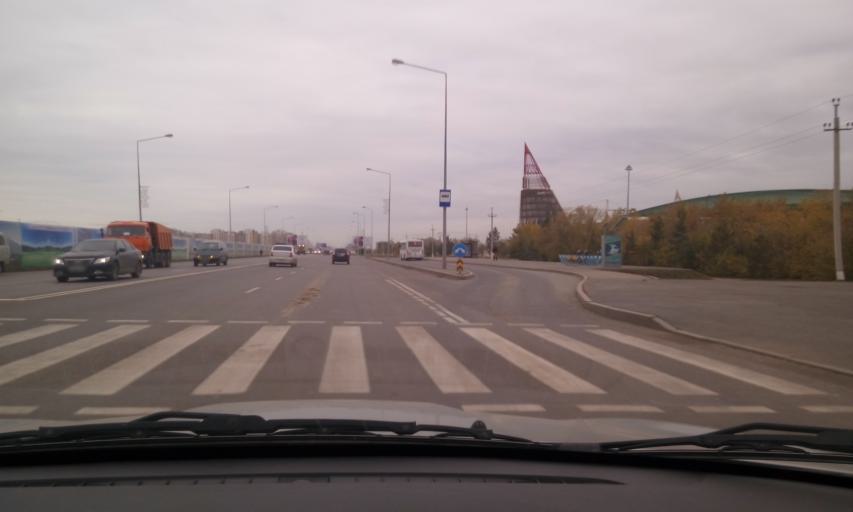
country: KZ
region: Astana Qalasy
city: Astana
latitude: 51.1075
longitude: 71.4090
